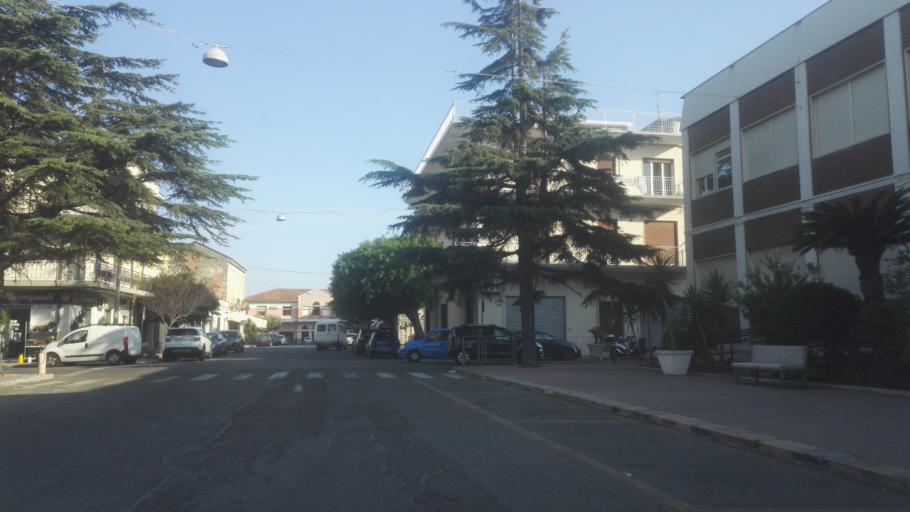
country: IT
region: Calabria
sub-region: Provincia di Reggio Calabria
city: Marina di Gioiosa Ionica
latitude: 38.3012
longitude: 16.3299
